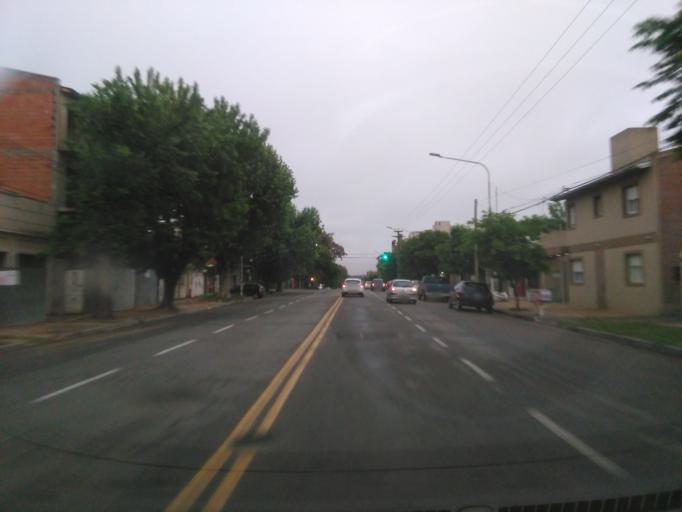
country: AR
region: Buenos Aires
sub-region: Partido de Tandil
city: Tandil
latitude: -37.3314
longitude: -59.1438
